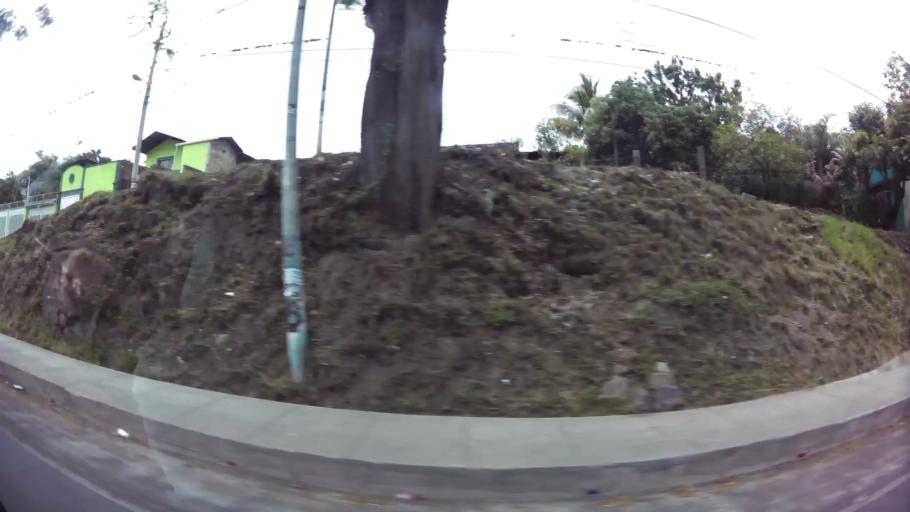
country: NI
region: Matagalpa
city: Matagalpa
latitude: 12.9374
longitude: -85.9155
